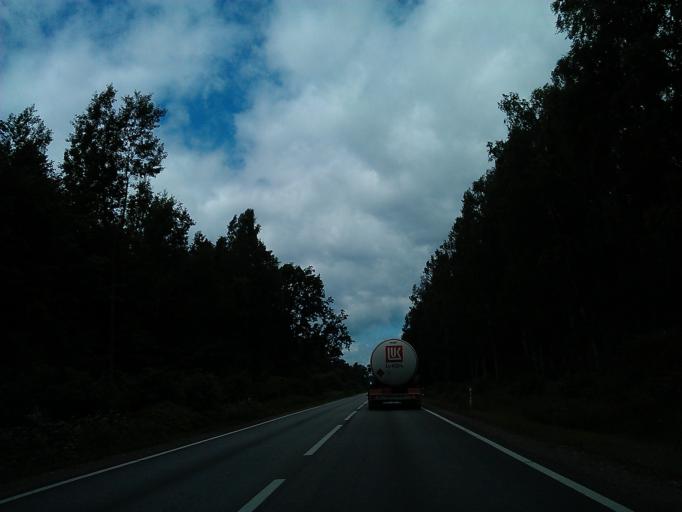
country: LV
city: Tireli
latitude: 56.9279
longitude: 23.5692
